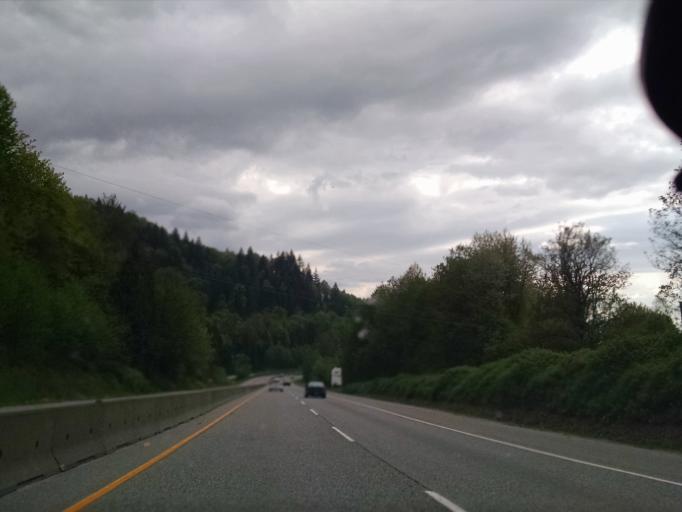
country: CA
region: British Columbia
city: Agassiz
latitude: 49.1632
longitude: -121.7938
